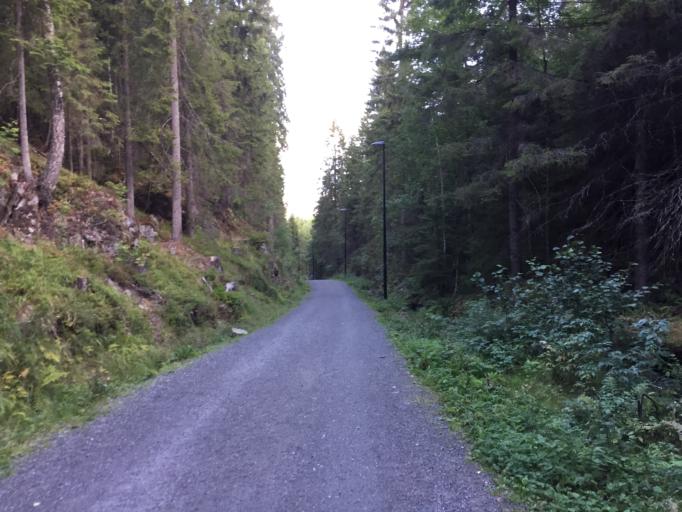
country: NO
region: Akershus
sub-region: Skedsmo
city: Lillestrom
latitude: 59.9269
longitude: 11.0284
